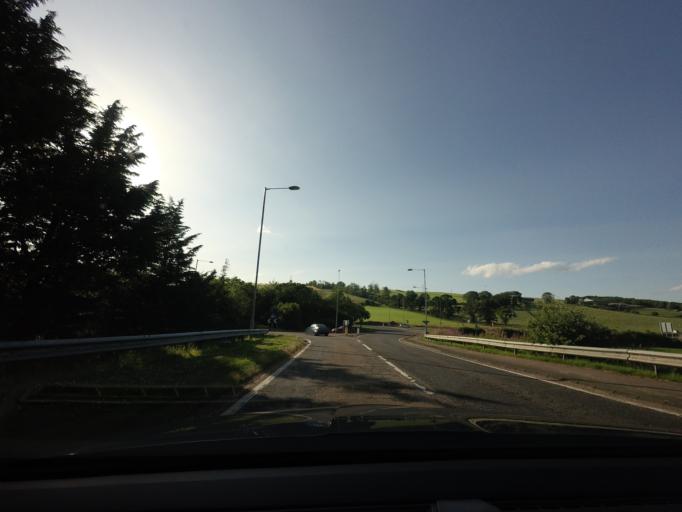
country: GB
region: Scotland
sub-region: Highland
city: Conon Bridge
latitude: 57.5788
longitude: -4.4367
